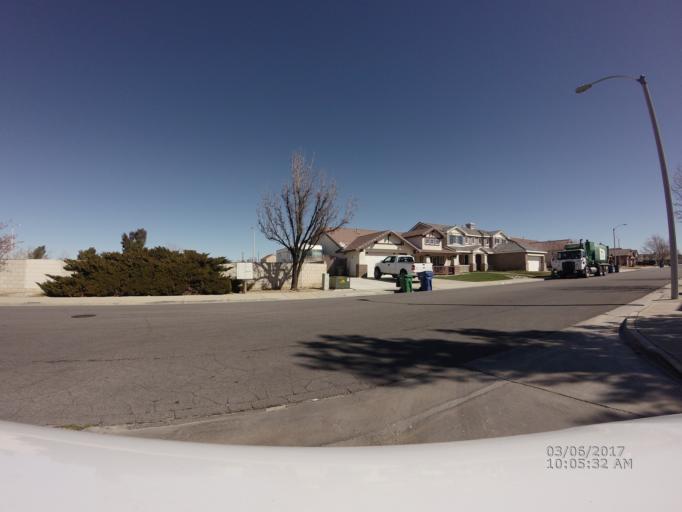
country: US
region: California
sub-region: Los Angeles County
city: Quartz Hill
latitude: 34.6523
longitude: -118.2037
